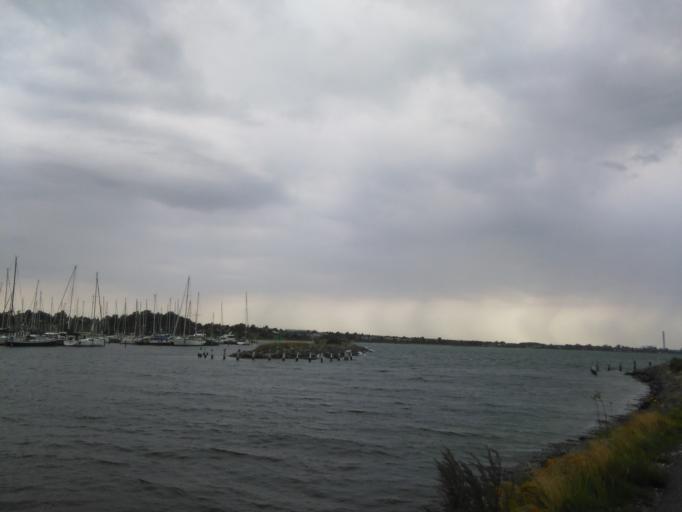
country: DK
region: Central Jutland
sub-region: Arhus Kommune
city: Hjortshoj
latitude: 56.2085
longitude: 10.2920
